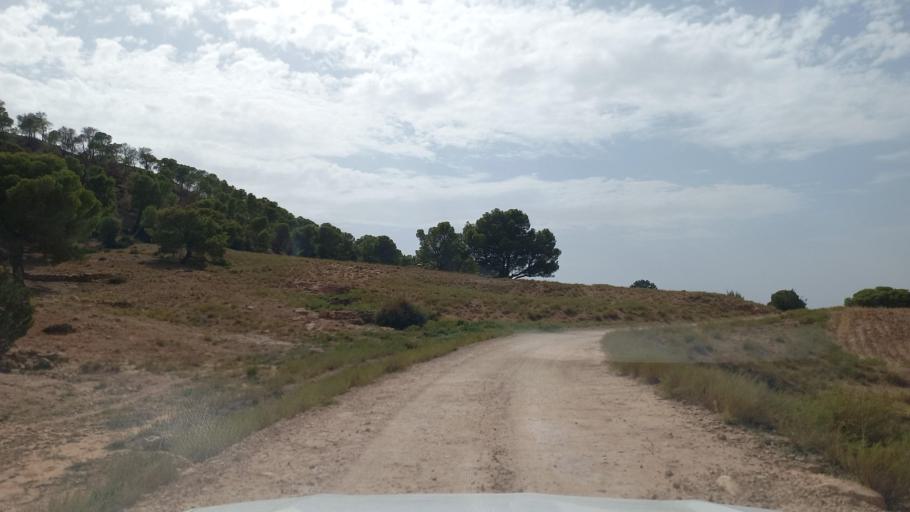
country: TN
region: Al Qasrayn
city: Kasserine
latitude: 35.3518
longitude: 8.8844
